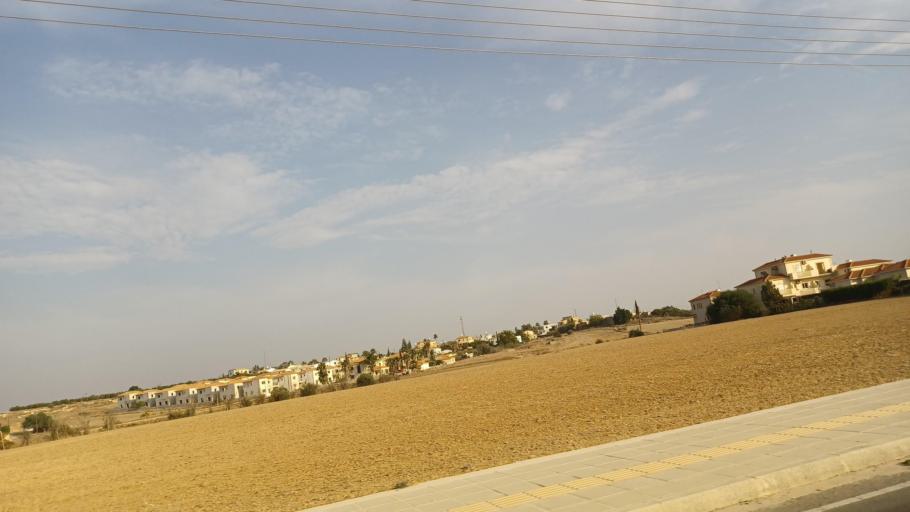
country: CY
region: Ammochostos
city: Acheritou
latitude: 35.0776
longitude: 33.8736
